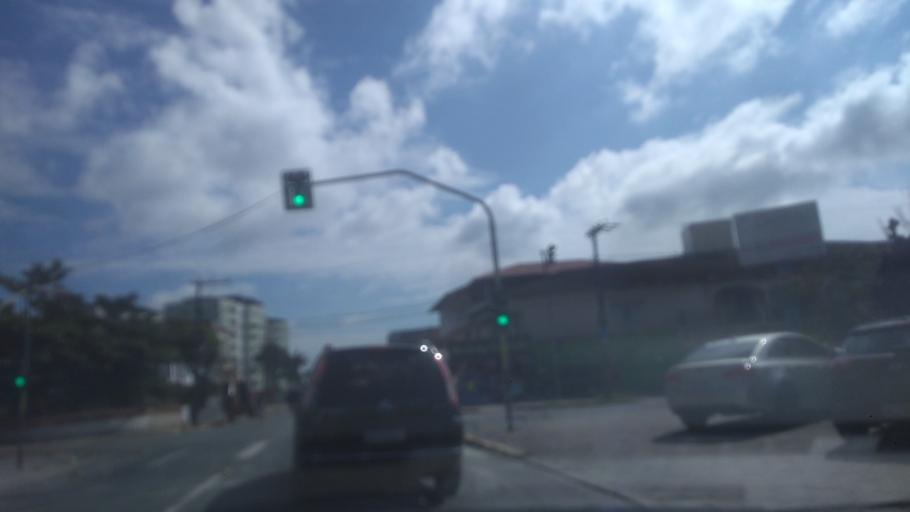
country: BR
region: Santa Catarina
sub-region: Joinville
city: Joinville
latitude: -26.3028
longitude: -48.8237
